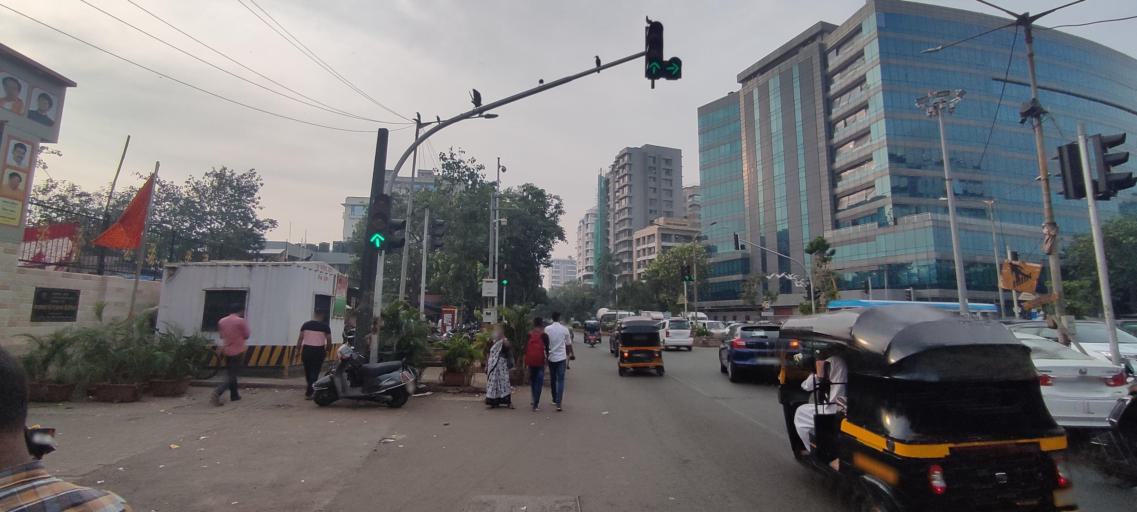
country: IN
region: Maharashtra
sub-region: Mumbai Suburban
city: Mumbai
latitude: 19.1024
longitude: 72.8370
